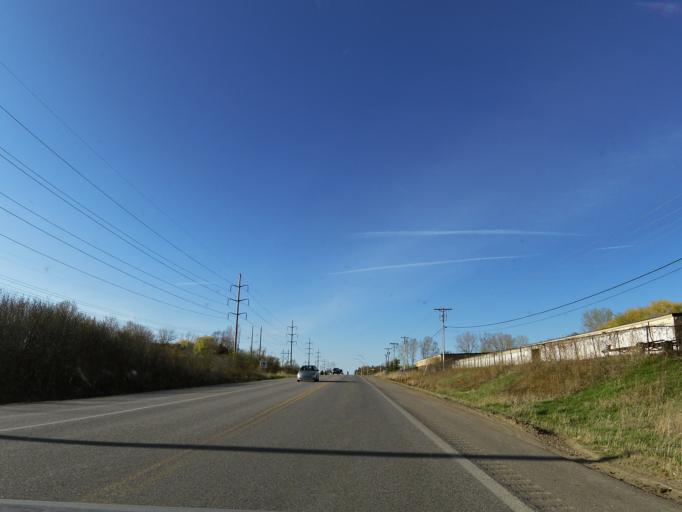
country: US
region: Minnesota
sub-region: Dakota County
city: Lakeville
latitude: 44.6201
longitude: -93.2931
